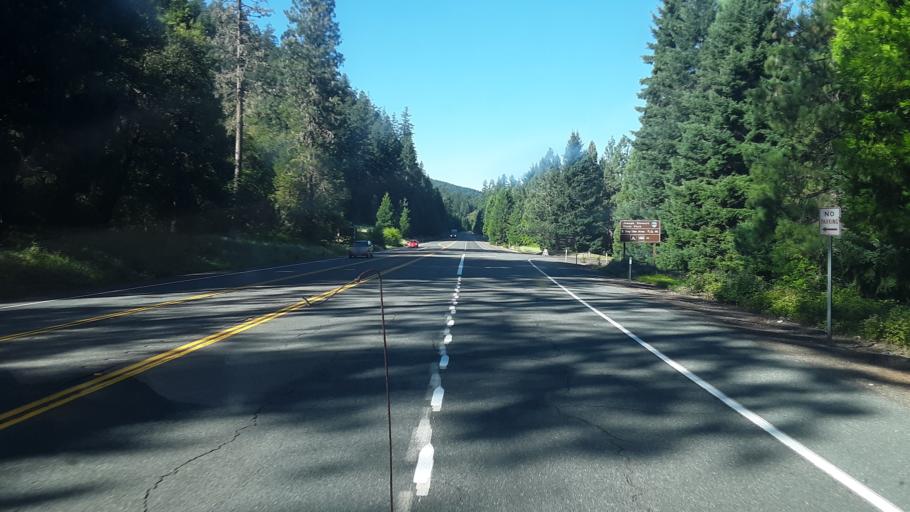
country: US
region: Oregon
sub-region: Jackson County
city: Shady Cove
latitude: 42.6834
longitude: -122.6128
